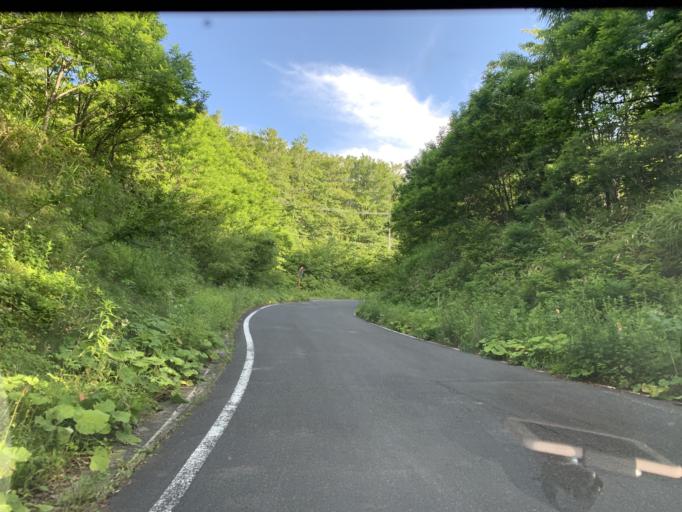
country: JP
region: Iwate
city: Ichinoseki
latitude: 38.9069
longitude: 140.8441
